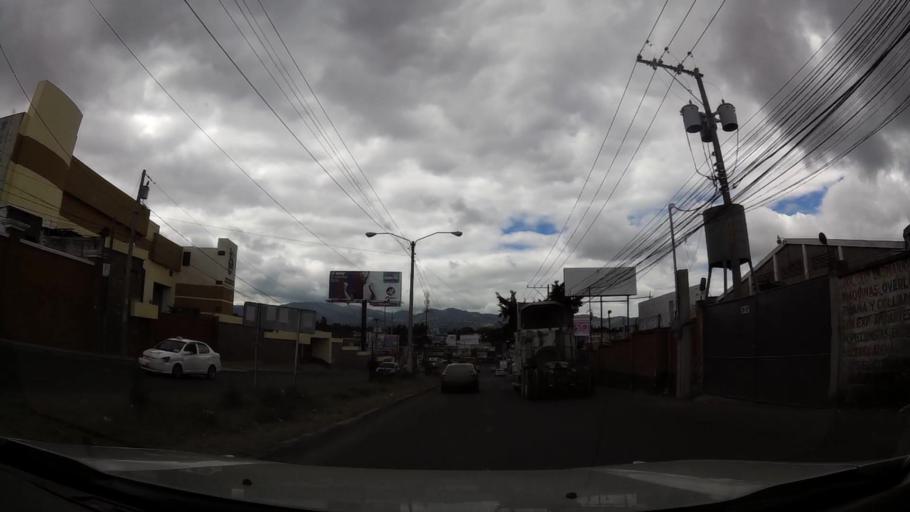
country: GT
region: Guatemala
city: Mixco
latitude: 14.6601
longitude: -90.5619
